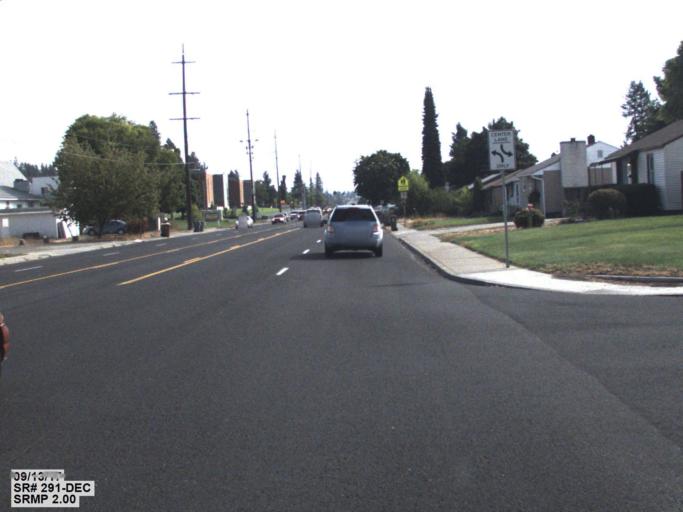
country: US
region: Washington
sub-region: Spokane County
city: Town and Country
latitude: 47.7154
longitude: -117.4540
